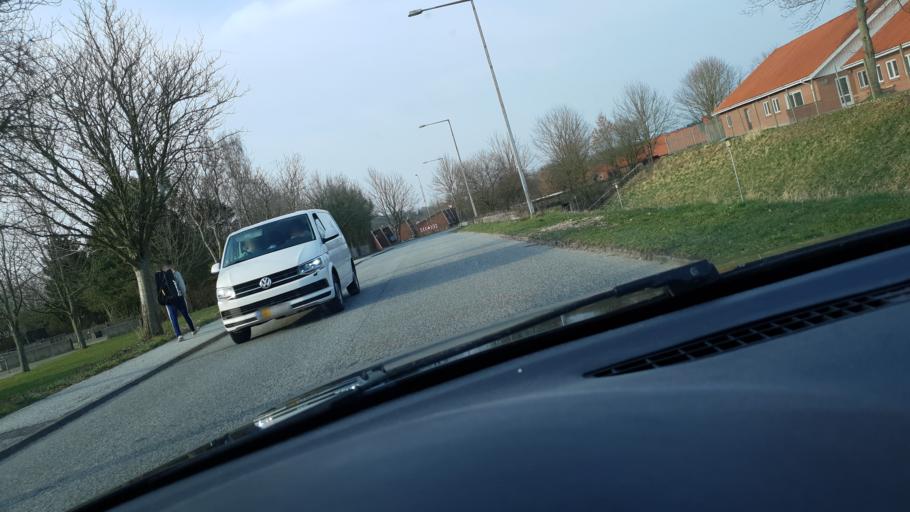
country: DK
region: South Denmark
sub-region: Fredericia Kommune
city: Snoghoj
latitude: 55.5484
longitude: 9.7052
